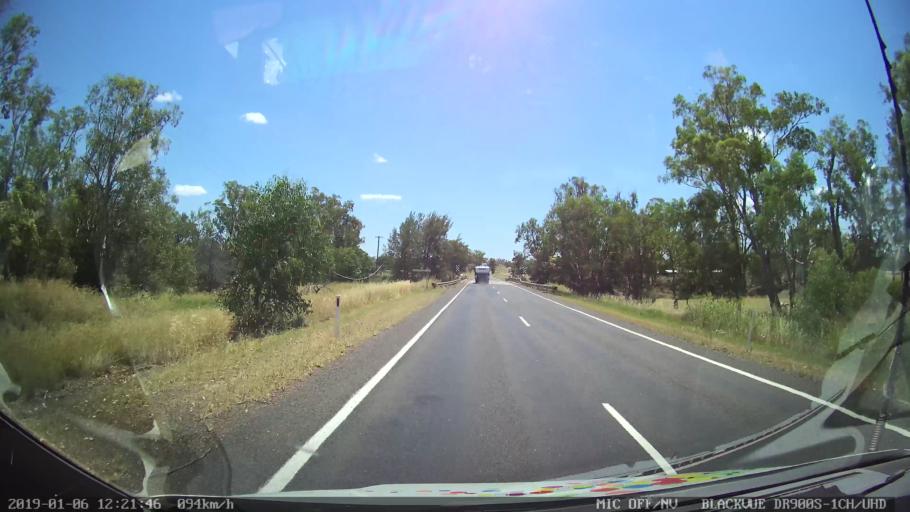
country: AU
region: New South Wales
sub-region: Tamworth Municipality
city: Phillip
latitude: -31.2705
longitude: 150.7848
